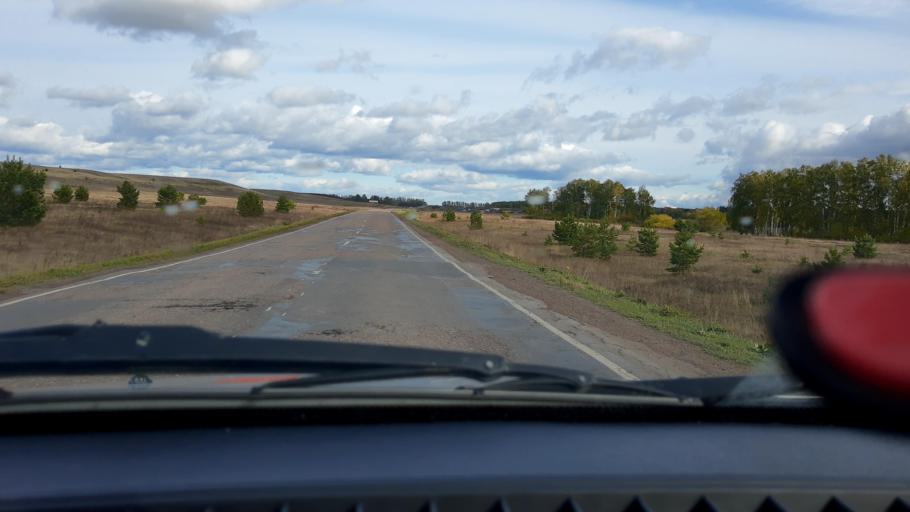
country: RU
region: Bashkortostan
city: Aksakovo
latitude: 54.0187
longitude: 54.1795
